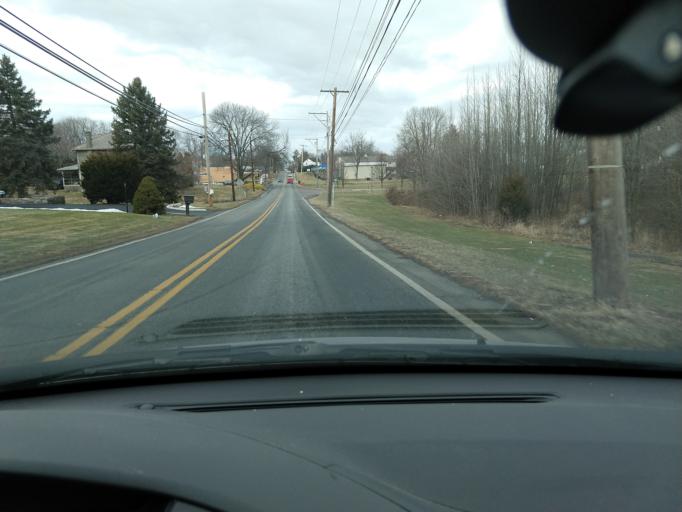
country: US
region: Pennsylvania
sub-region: Chester County
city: South Pottstown
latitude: 40.2256
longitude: -75.6560
